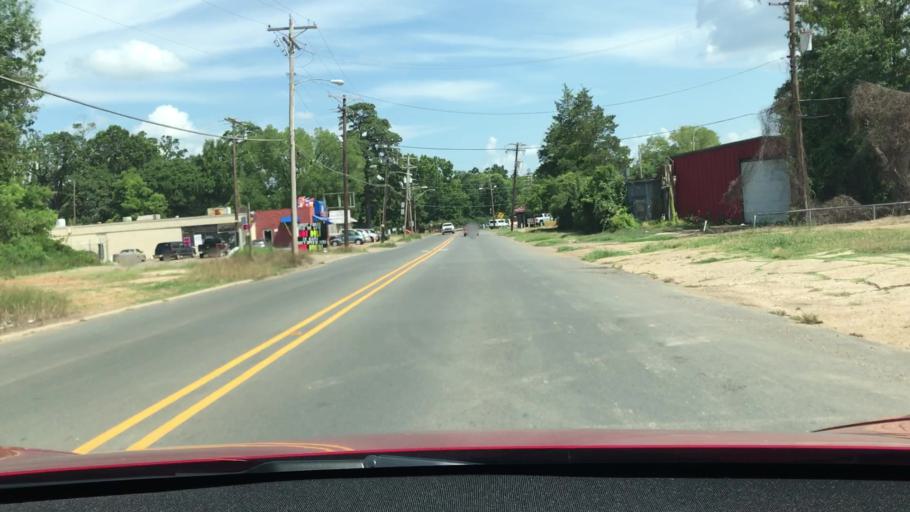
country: US
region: Louisiana
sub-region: Bossier Parish
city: Bossier City
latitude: 32.5016
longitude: -93.7345
